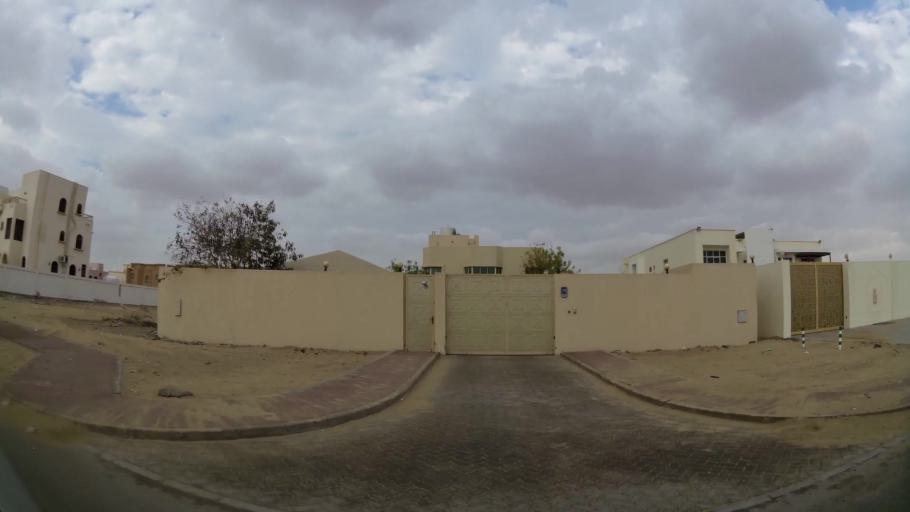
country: AE
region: Abu Dhabi
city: Abu Dhabi
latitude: 24.3434
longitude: 54.6149
